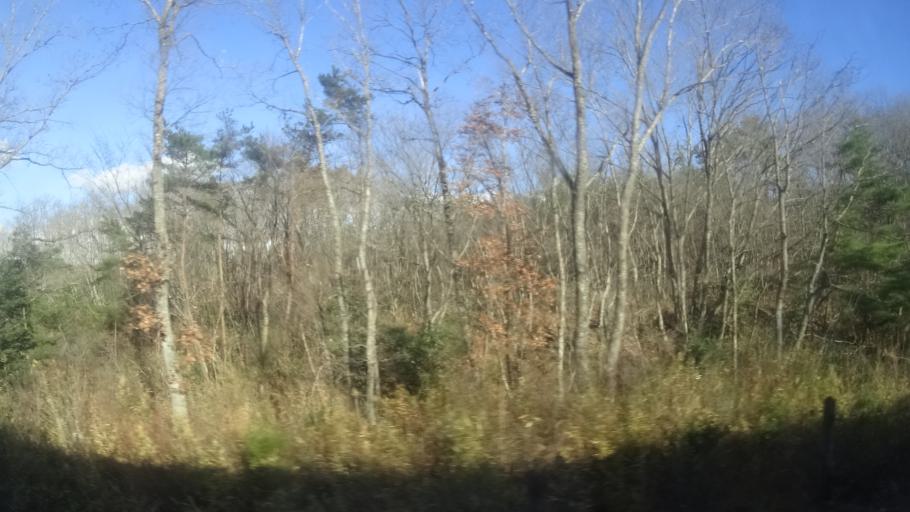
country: JP
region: Miyagi
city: Marumori
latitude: 37.7449
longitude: 140.9426
